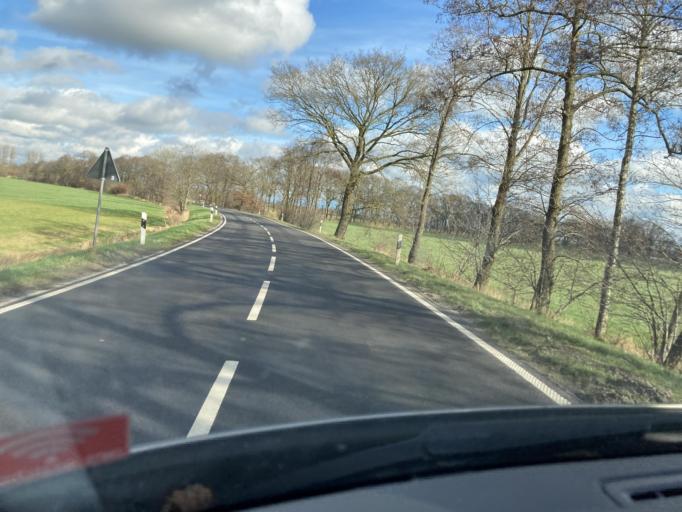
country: DE
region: Lower Saxony
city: Ostrhauderfehn
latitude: 53.1690
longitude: 7.5854
